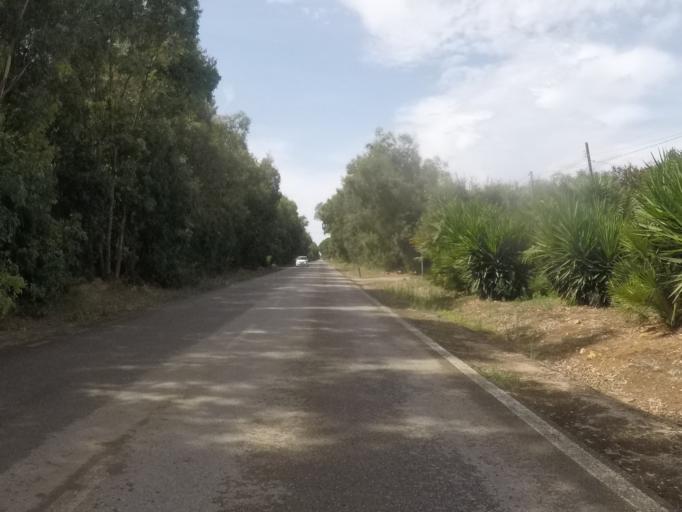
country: IT
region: Sardinia
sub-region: Provincia di Sassari
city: Alghero
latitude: 40.6560
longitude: 8.2330
